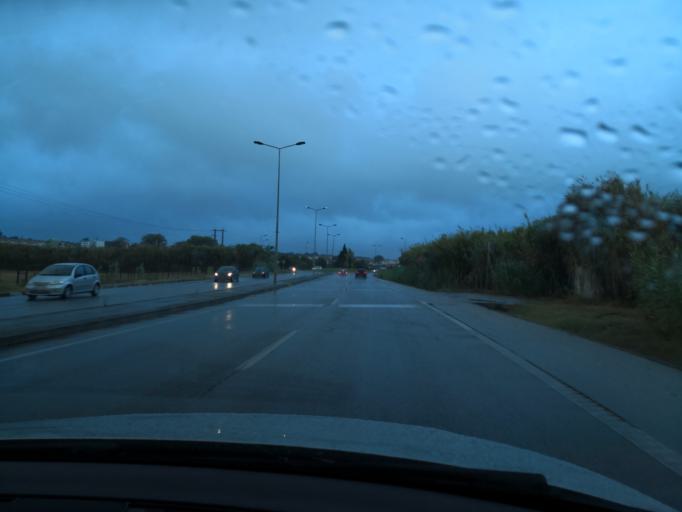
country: PT
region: Setubal
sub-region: Moita
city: Moita
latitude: 38.6507
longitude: -9.0015
